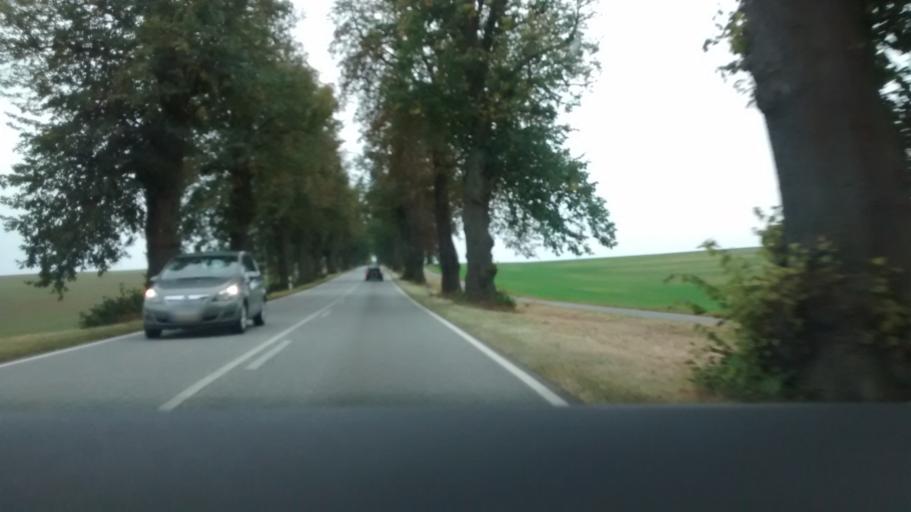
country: DE
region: Mecklenburg-Vorpommern
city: Mecklenburg
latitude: 53.8372
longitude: 11.4573
